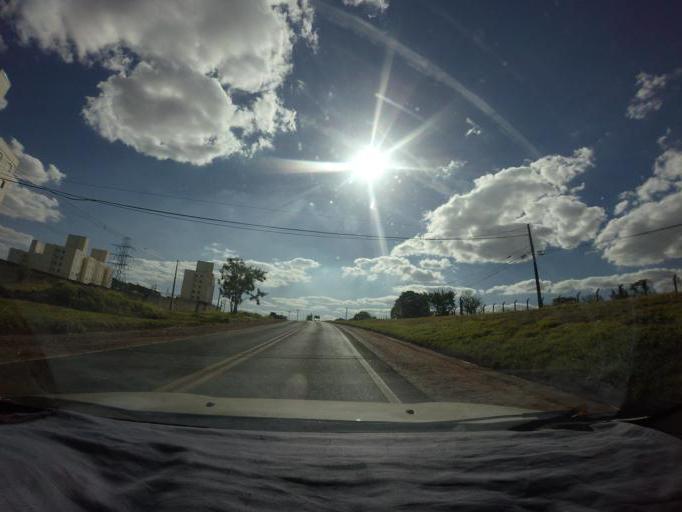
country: BR
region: Sao Paulo
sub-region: Piracicaba
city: Piracicaba
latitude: -22.7398
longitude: -47.5876
